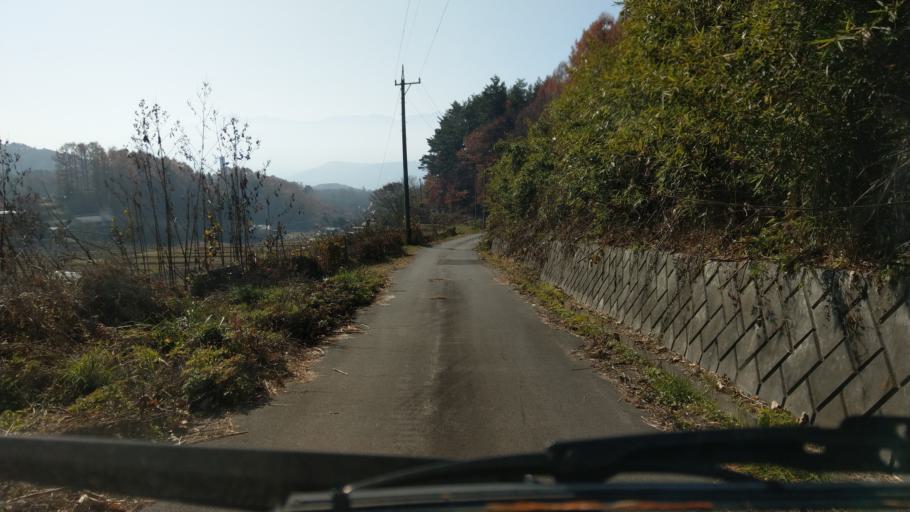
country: JP
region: Nagano
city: Komoro
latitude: 36.3583
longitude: 138.4378
